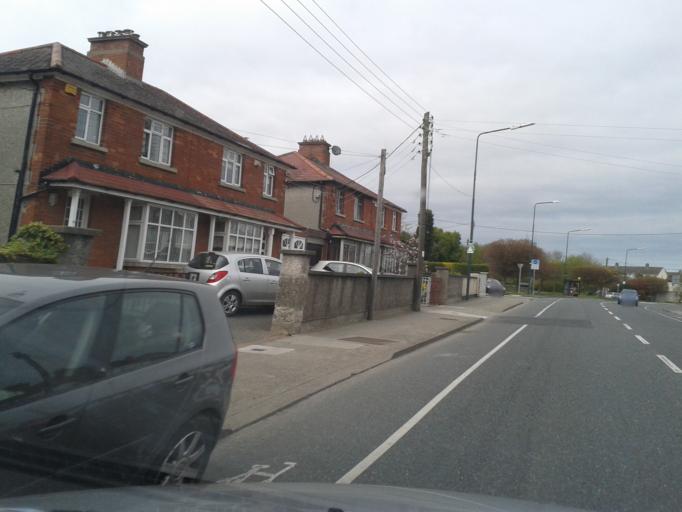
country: IE
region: Leinster
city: Beaumont
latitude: 53.3834
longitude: -6.2373
